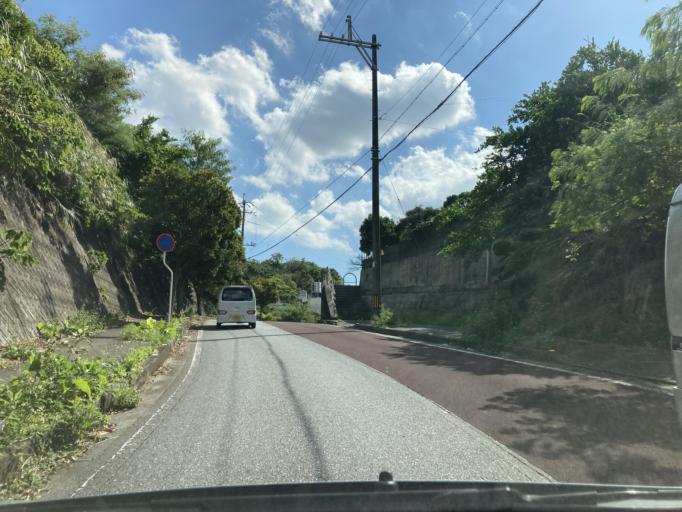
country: JP
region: Okinawa
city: Ginowan
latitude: 26.2454
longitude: 127.7558
